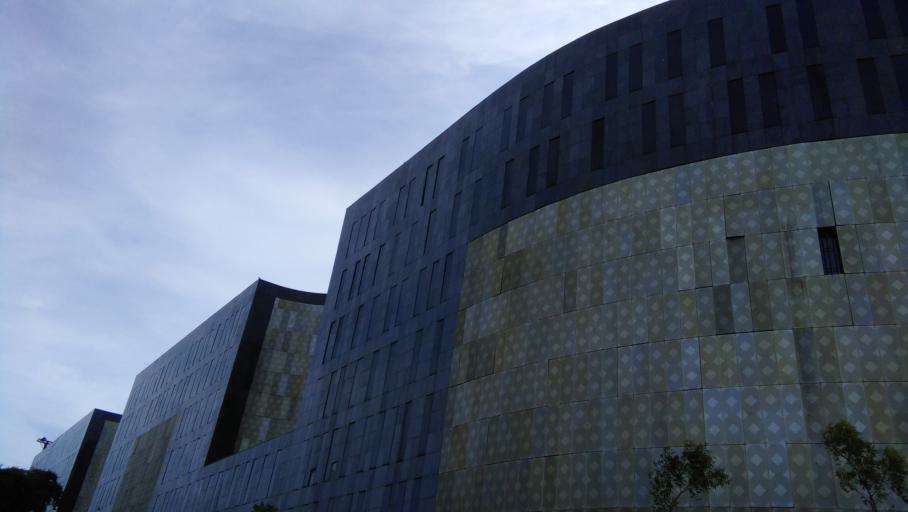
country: IN
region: Tamil Nadu
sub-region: Chennai
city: Chennai
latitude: 13.0699
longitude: 80.2749
